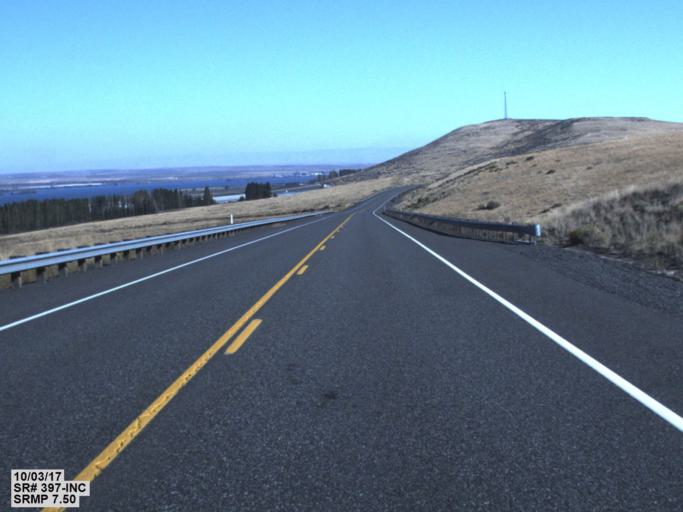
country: US
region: Washington
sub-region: Benton County
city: Finley
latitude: 46.1258
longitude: -119.0614
